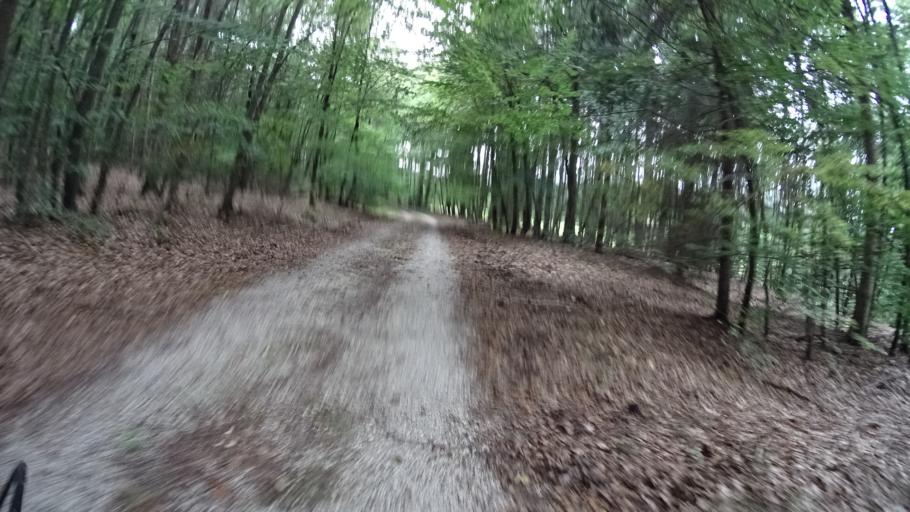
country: DE
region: Bavaria
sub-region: Upper Bavaria
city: Walting
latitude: 48.9151
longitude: 11.3125
